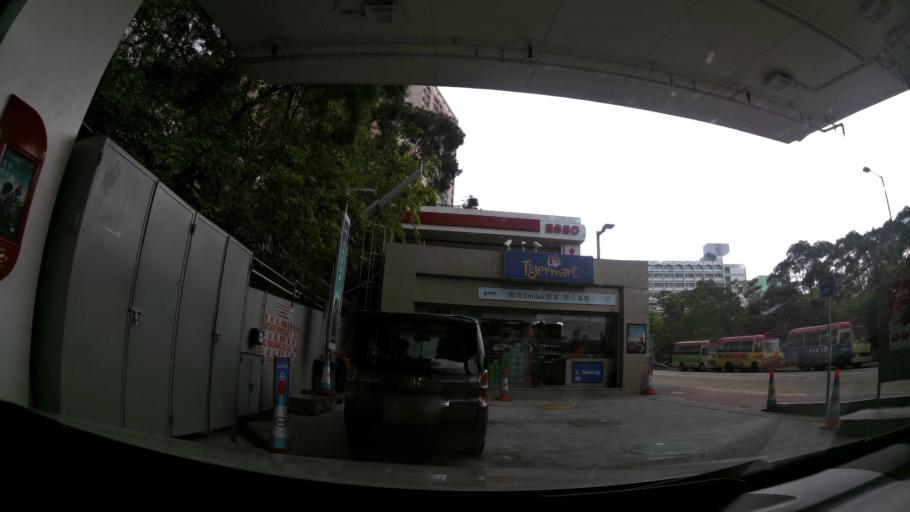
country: HK
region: Kowloon City
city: Kowloon
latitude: 22.3160
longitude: 114.2326
